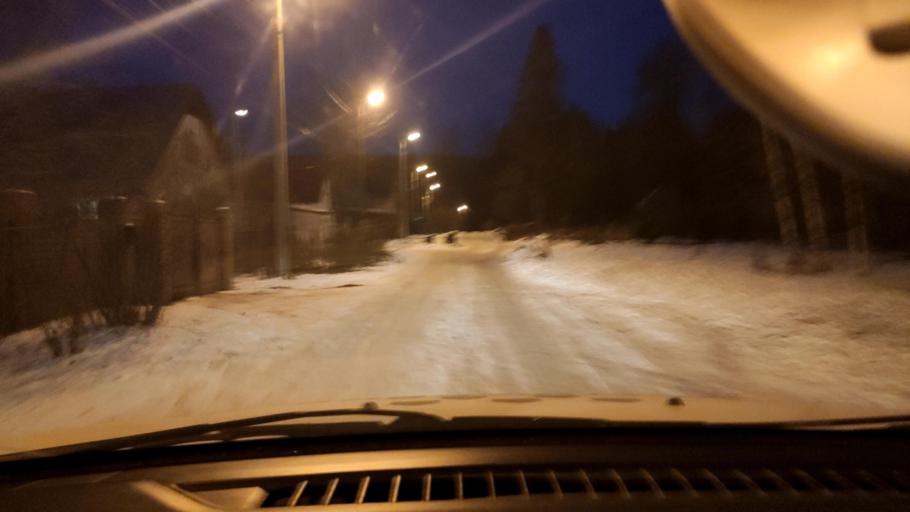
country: RU
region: Perm
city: Kondratovo
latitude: 58.0485
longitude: 56.1097
